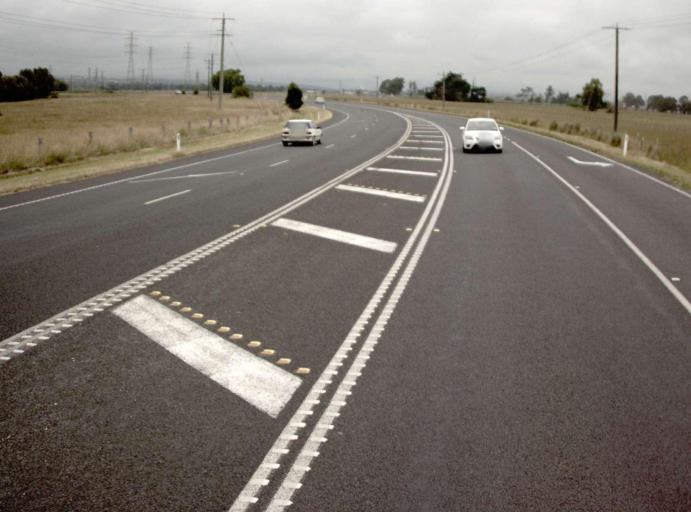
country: AU
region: Victoria
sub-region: Latrobe
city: Morwell
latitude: -38.2699
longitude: 146.4235
